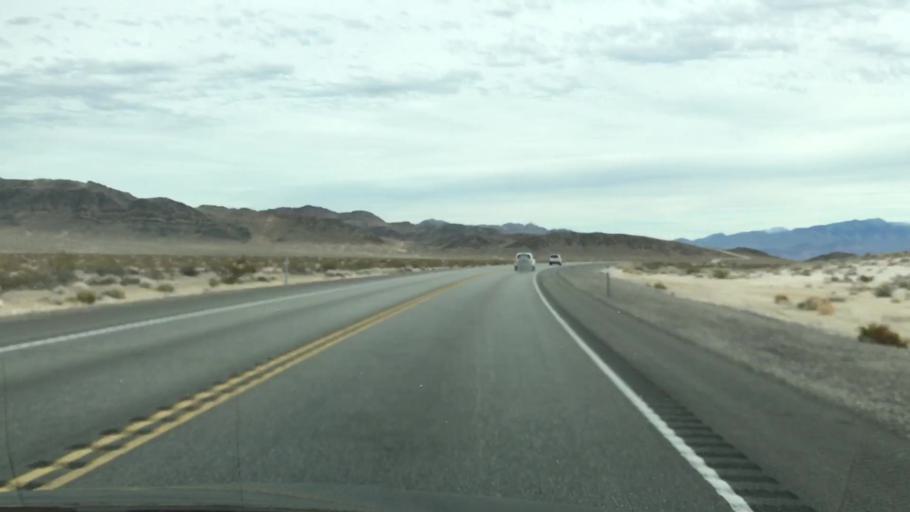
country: US
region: Nevada
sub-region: Nye County
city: Beatty
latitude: 36.6314
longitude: -116.3206
